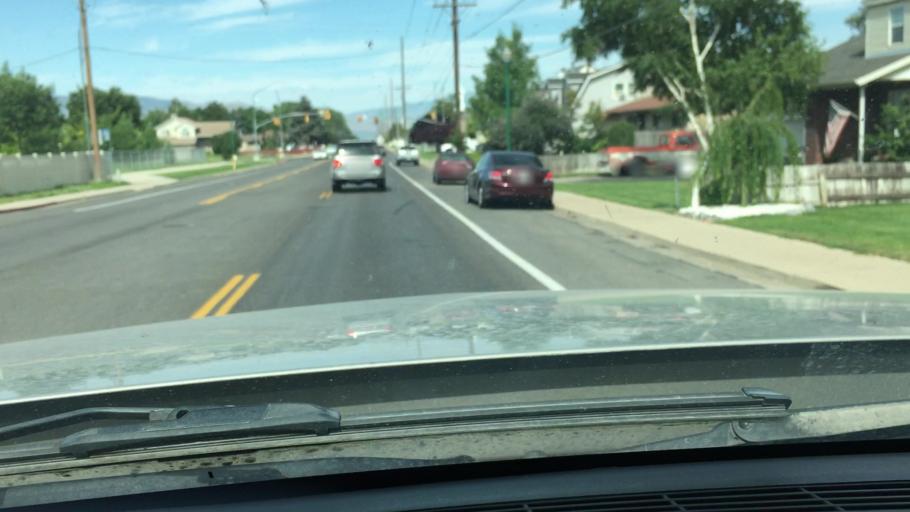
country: US
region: Utah
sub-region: Utah County
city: Lindon
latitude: 40.3265
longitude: -111.7135
